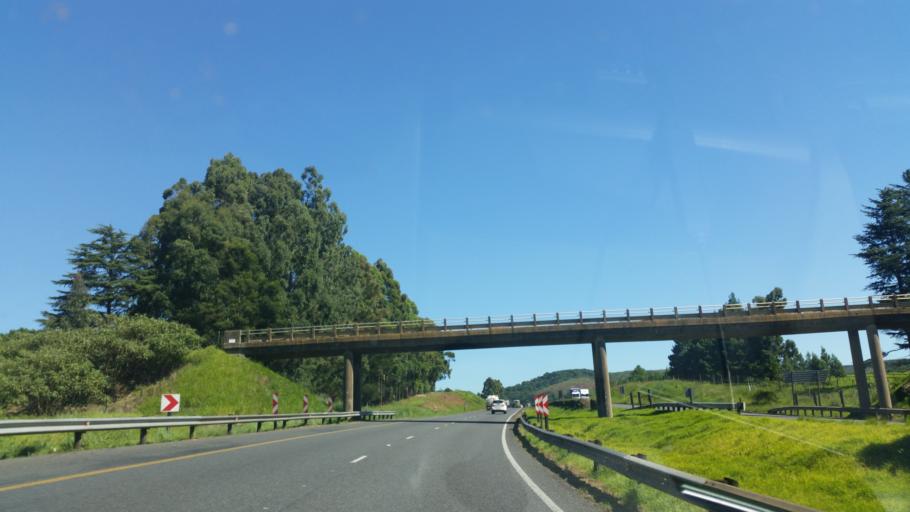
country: ZA
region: KwaZulu-Natal
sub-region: uMgungundlovu District Municipality
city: Mooirivier
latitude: -29.3543
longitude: 30.0887
